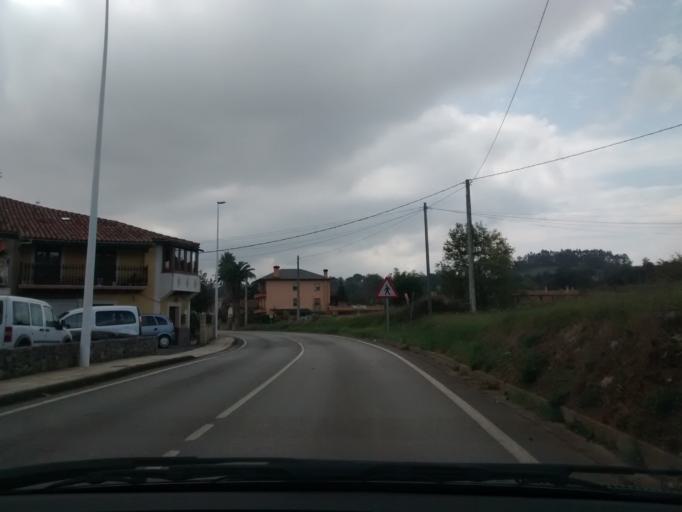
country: ES
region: Cantabria
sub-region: Provincia de Cantabria
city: Entrambasaguas
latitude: 43.3693
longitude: -3.6939
